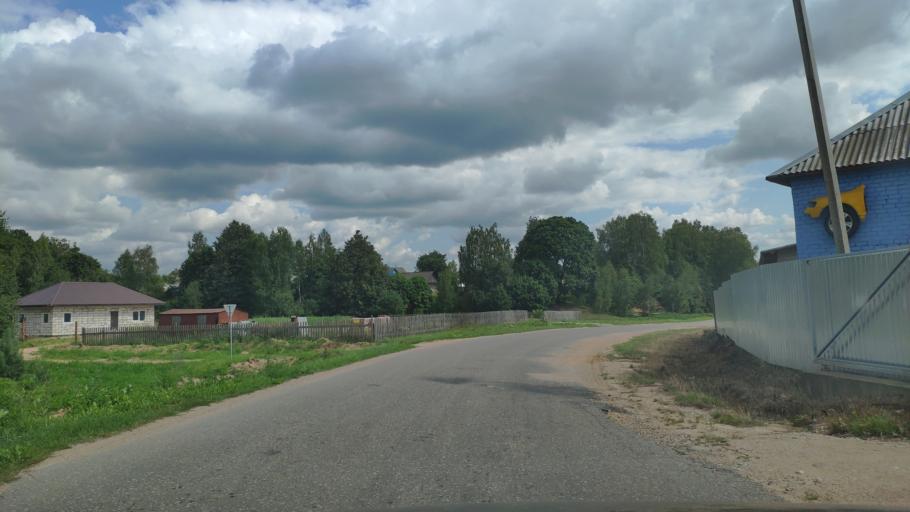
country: BY
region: Minsk
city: Khatsyezhyna
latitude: 53.8538
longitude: 27.3076
